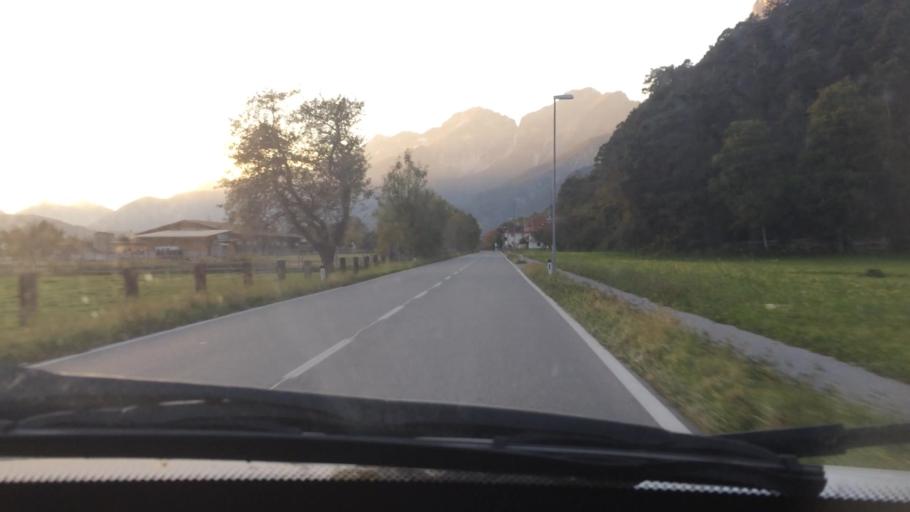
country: AT
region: Tyrol
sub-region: Politischer Bezirk Innsbruck Land
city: Pettnau
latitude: 47.3005
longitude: 11.1380
